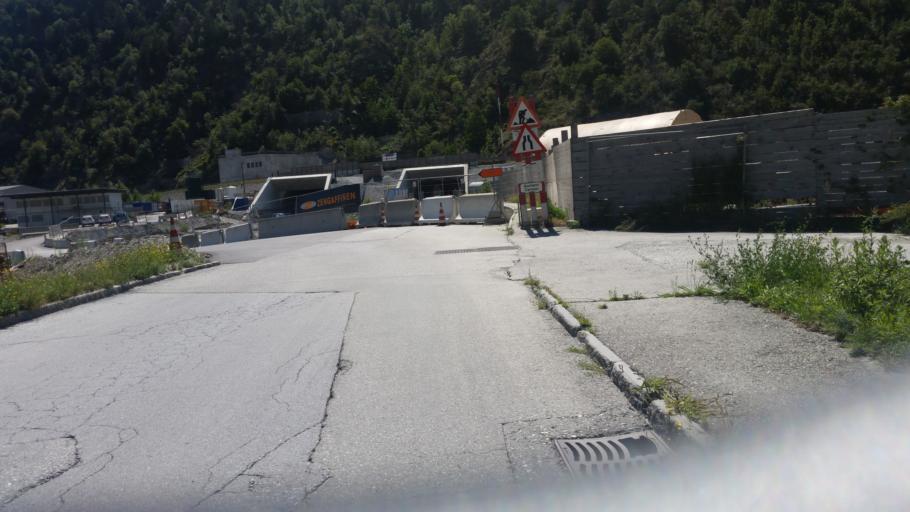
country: CH
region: Valais
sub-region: Visp District
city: Baltschieder
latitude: 46.2985
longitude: 7.8618
